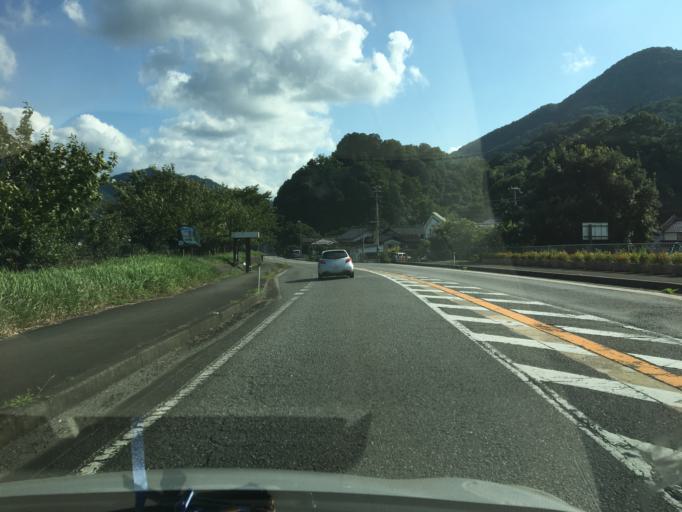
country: JP
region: Hyogo
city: Toyooka
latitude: 35.4346
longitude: 134.7890
